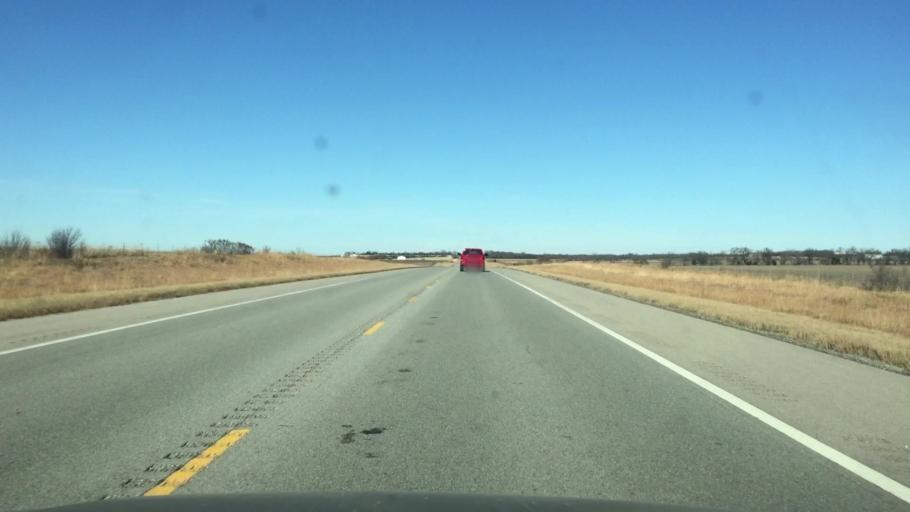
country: US
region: Kansas
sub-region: Allen County
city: Iola
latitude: 37.9530
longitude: -95.3812
